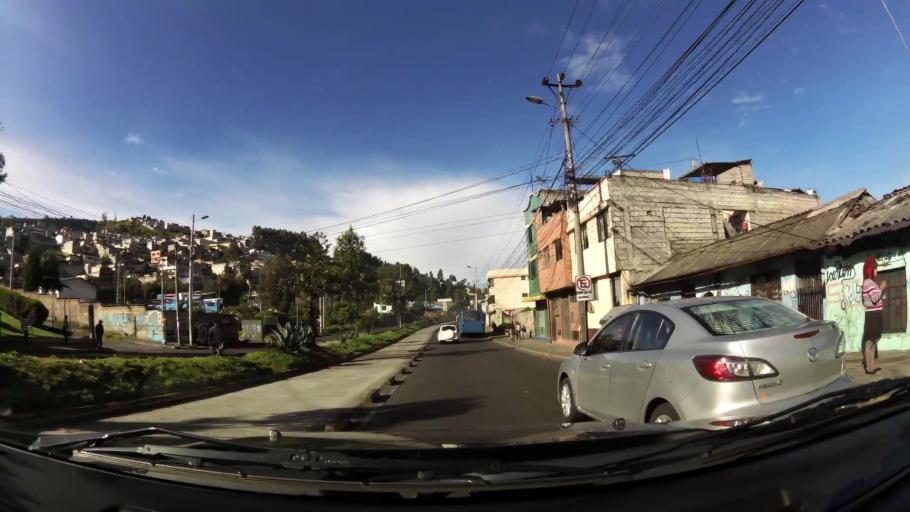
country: EC
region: Pichincha
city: Quito
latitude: -0.2748
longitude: -78.5300
